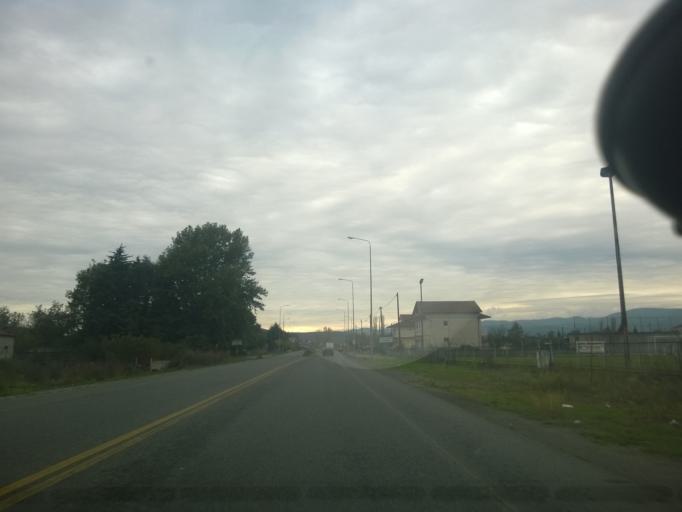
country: GR
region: Central Macedonia
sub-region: Nomos Pellis
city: Aridaia
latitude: 40.9367
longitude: 22.0842
